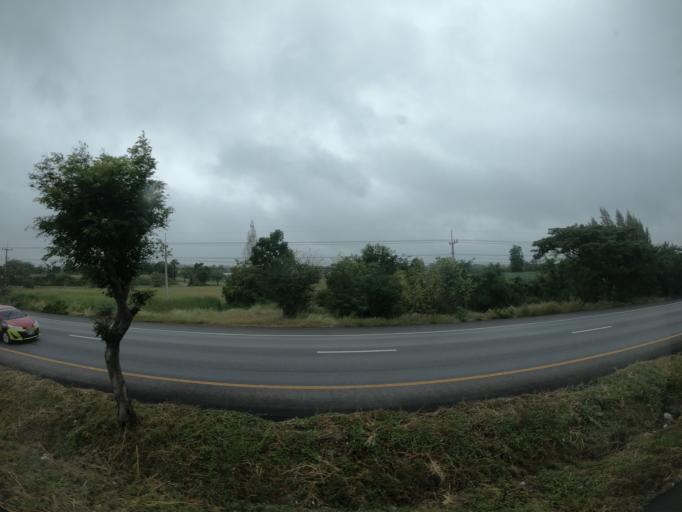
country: TH
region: Nakhon Ratchasima
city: Phimai
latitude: 15.3126
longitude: 102.4284
